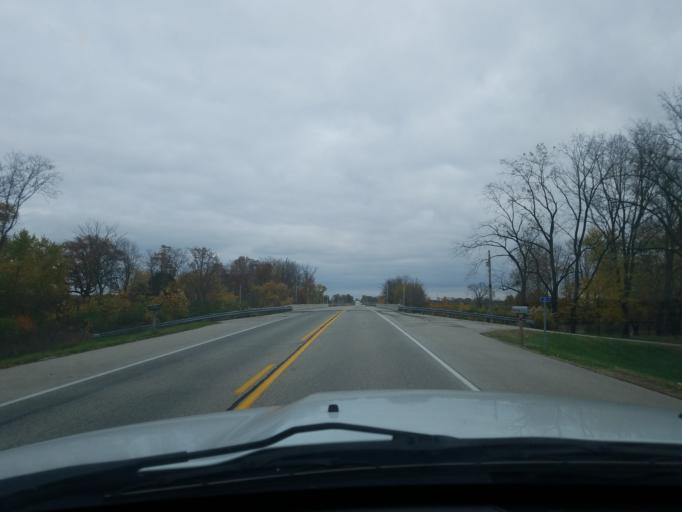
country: US
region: Indiana
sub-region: Johnson County
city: Franklin
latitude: 39.4952
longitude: -85.9505
